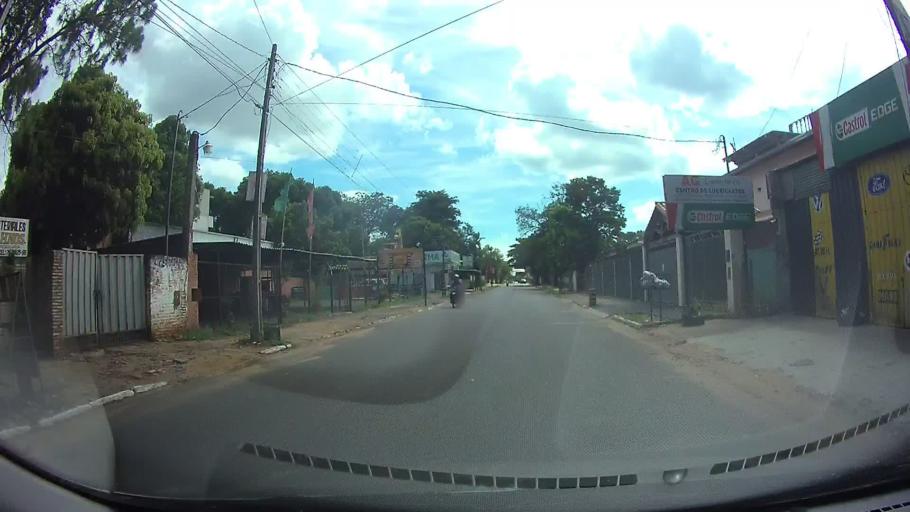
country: PY
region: Central
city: Villa Elisa
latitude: -25.3414
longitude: -57.5746
